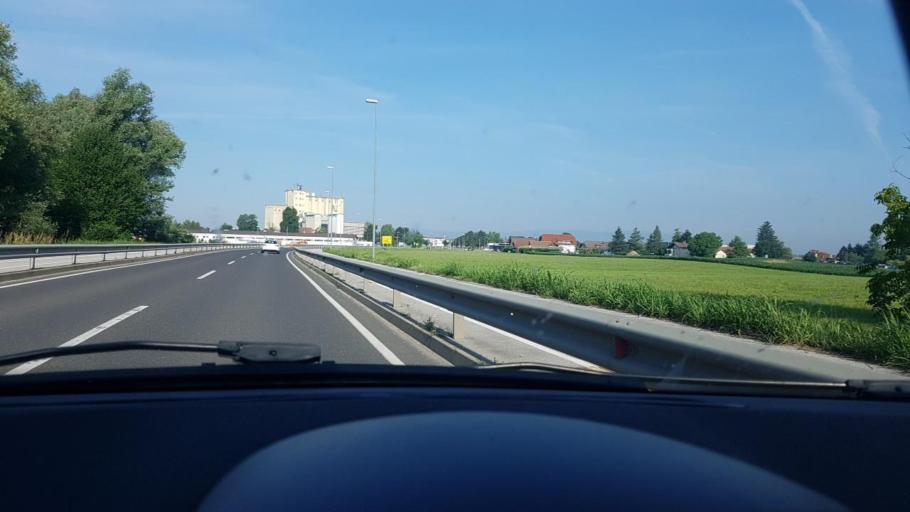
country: SI
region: Ptuj
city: Ptuj
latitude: 46.4065
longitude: 15.8710
